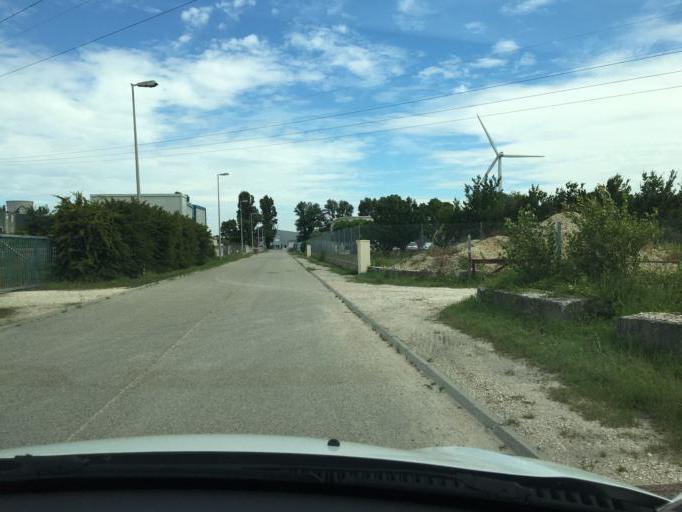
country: FR
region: Provence-Alpes-Cote d'Azur
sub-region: Departement du Vaucluse
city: Bollene
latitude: 44.3141
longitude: 4.7340
